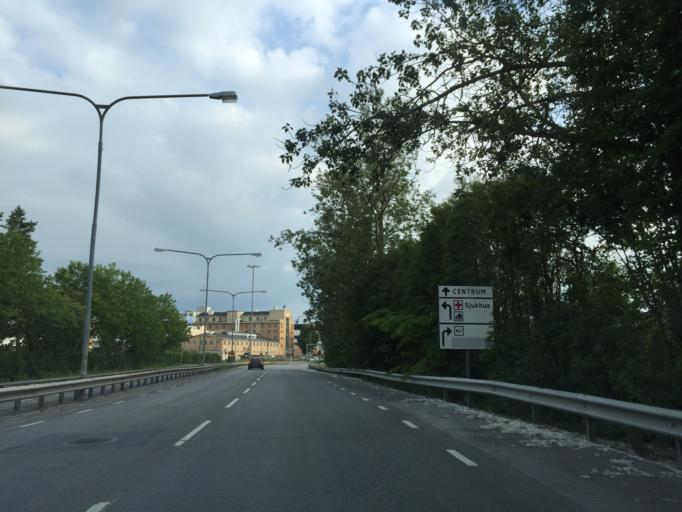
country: SE
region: OErebro
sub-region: Orebro Kommun
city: Orebro
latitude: 59.2811
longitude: 15.2150
